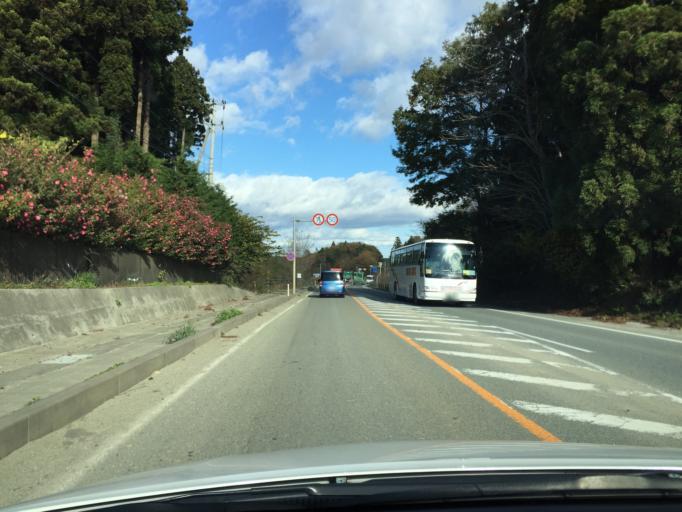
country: JP
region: Fukushima
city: Namie
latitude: 37.3661
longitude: 141.0091
